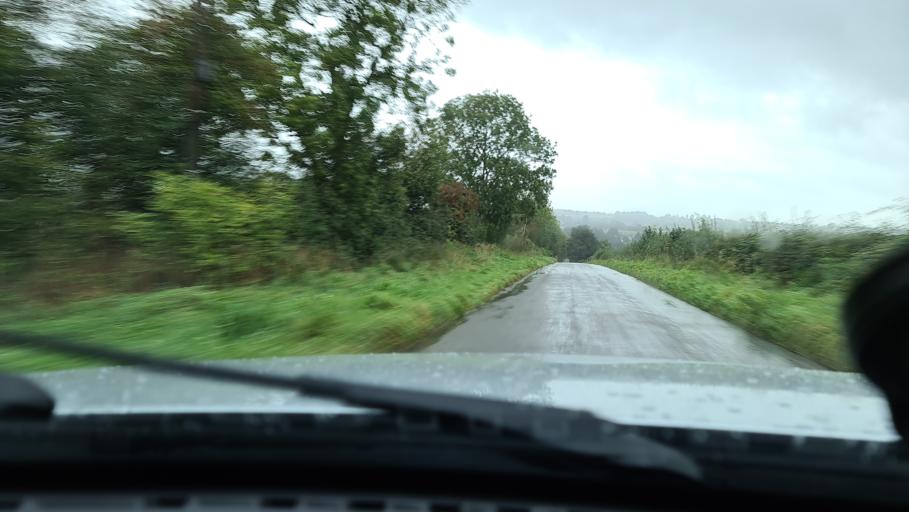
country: GB
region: England
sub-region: Oxfordshire
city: Deddington
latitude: 51.9225
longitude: -1.3674
